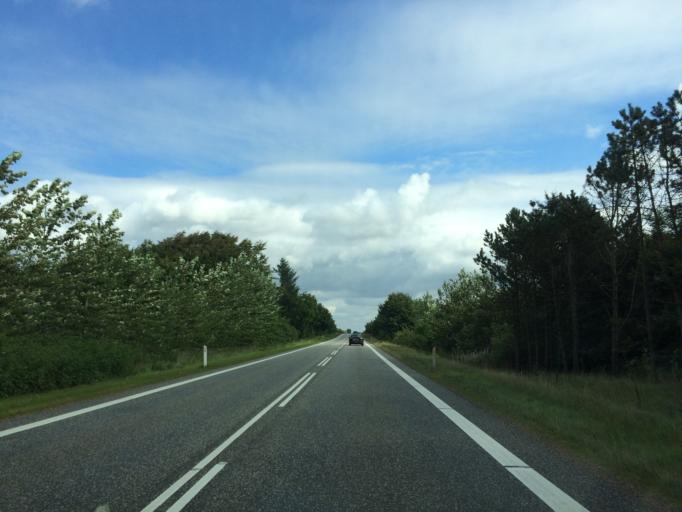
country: DK
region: Central Jutland
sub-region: Holstebro Kommune
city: Vinderup
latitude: 56.3738
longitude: 8.7468
